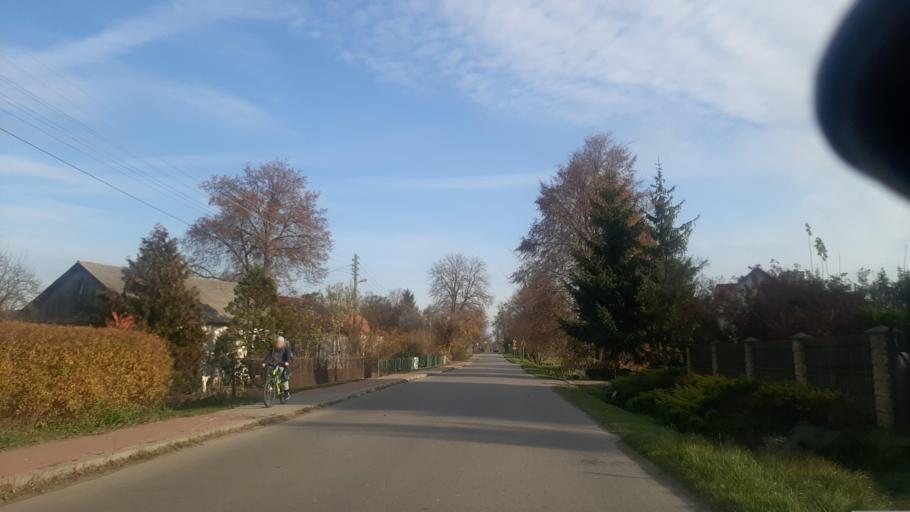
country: PL
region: Lublin Voivodeship
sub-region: Powiat lubelski
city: Garbow
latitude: 51.3829
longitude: 22.3822
